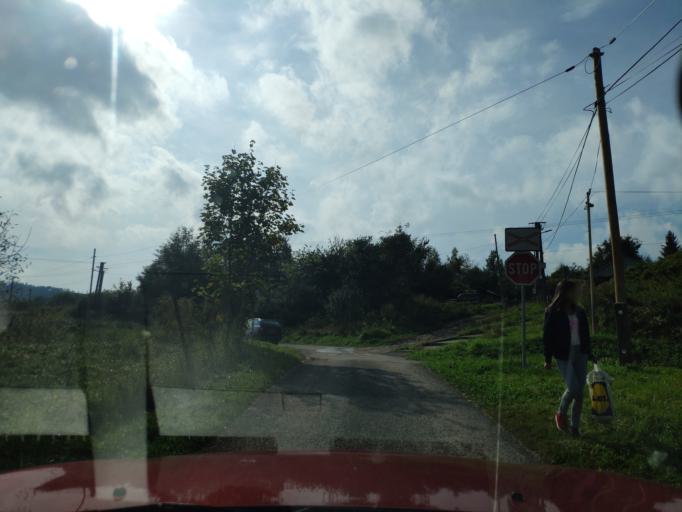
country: SK
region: Kosicky
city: Dobsina
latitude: 48.7108
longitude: 20.2810
